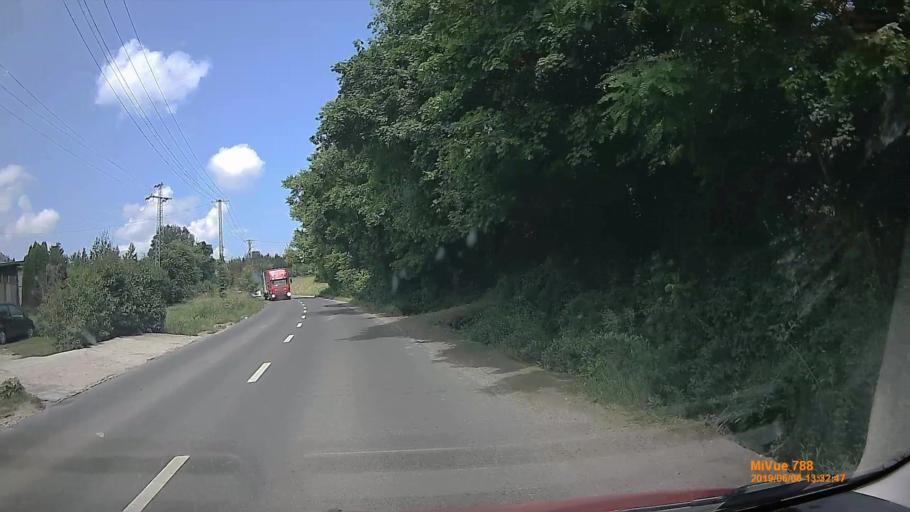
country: HU
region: Pest
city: Vac
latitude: 47.7873
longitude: 19.1462
